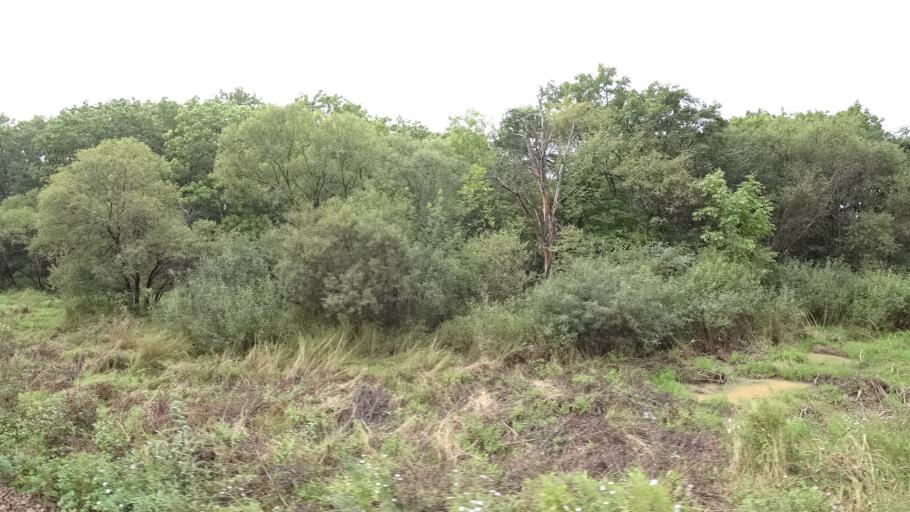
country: RU
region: Primorskiy
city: Lyalichi
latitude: 44.0803
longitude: 132.4510
